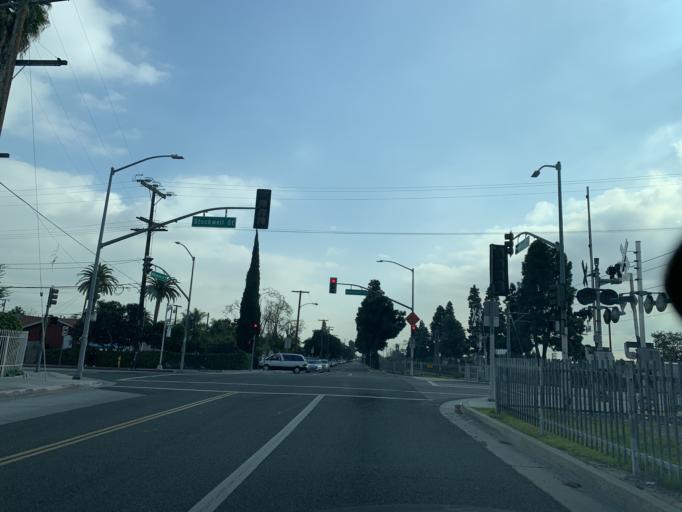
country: US
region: California
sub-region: Los Angeles County
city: Compton
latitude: 33.9112
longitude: -118.2286
